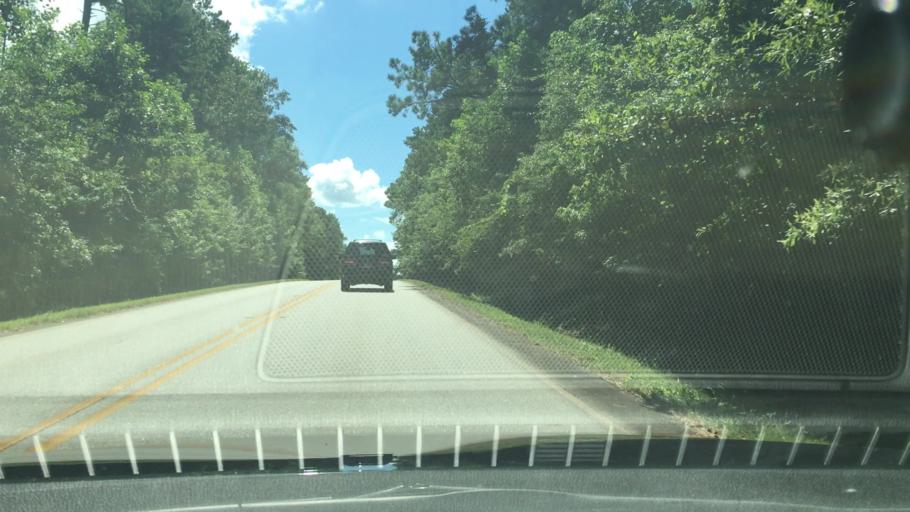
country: US
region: Georgia
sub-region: Jasper County
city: Monticello
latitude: 33.3006
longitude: -83.6592
